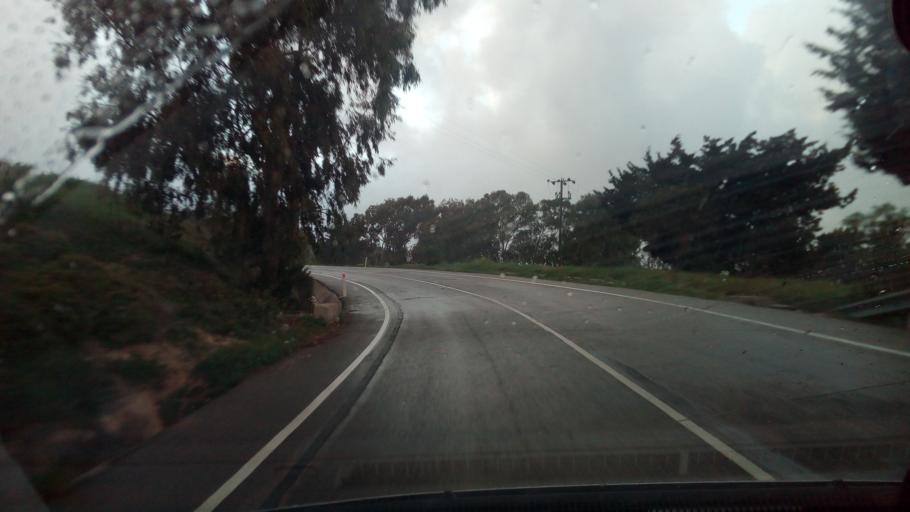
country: CY
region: Pafos
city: Polis
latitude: 34.9617
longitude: 32.4099
